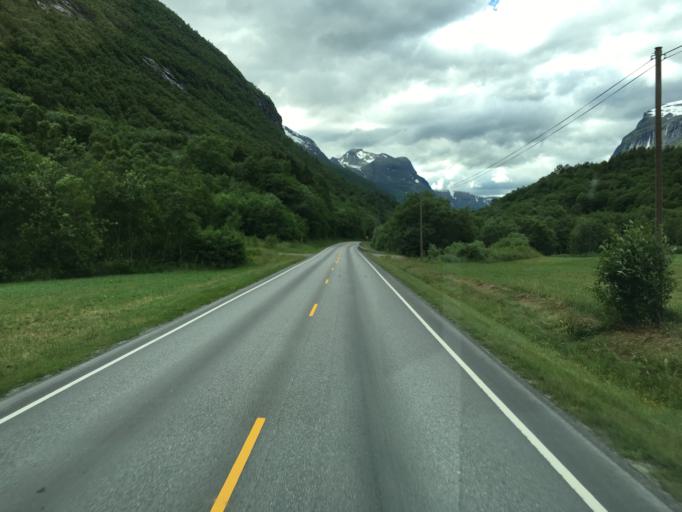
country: NO
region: More og Romsdal
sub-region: Sunndal
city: Sunndalsora
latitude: 62.6409
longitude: 8.7687
